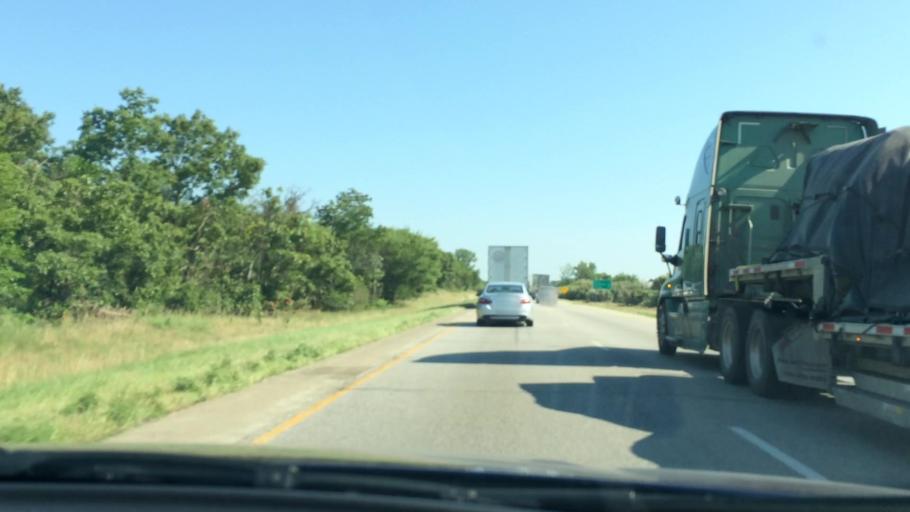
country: US
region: Indiana
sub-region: Newton County
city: Roselawn
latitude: 41.0244
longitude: -87.2706
